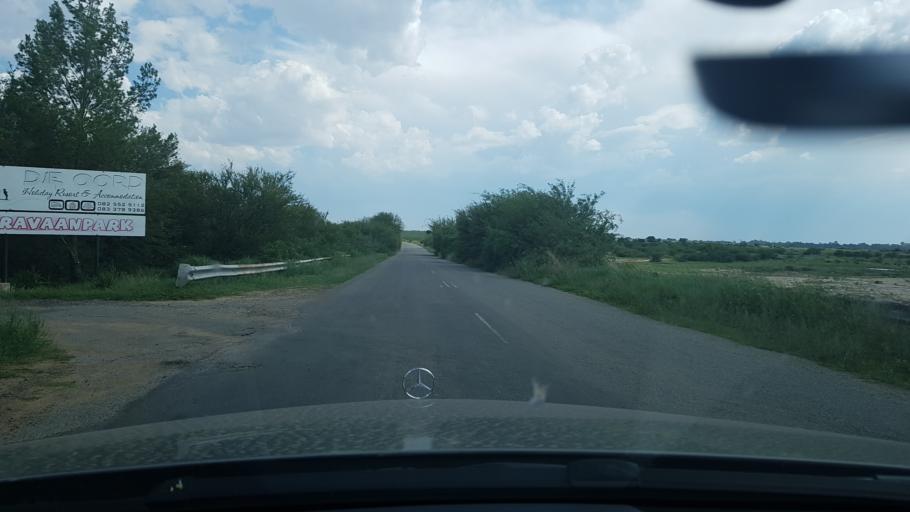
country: ZA
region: North-West
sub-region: Dr Ruth Segomotsi Mompati District Municipality
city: Bloemhof
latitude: -27.6564
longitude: 25.5948
